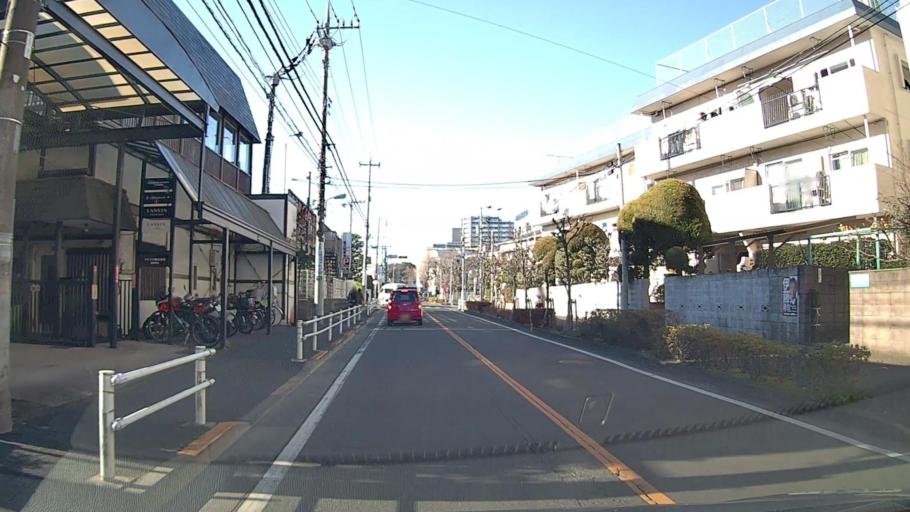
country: JP
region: Tokyo
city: Chofugaoka
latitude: 35.6584
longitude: 139.5671
